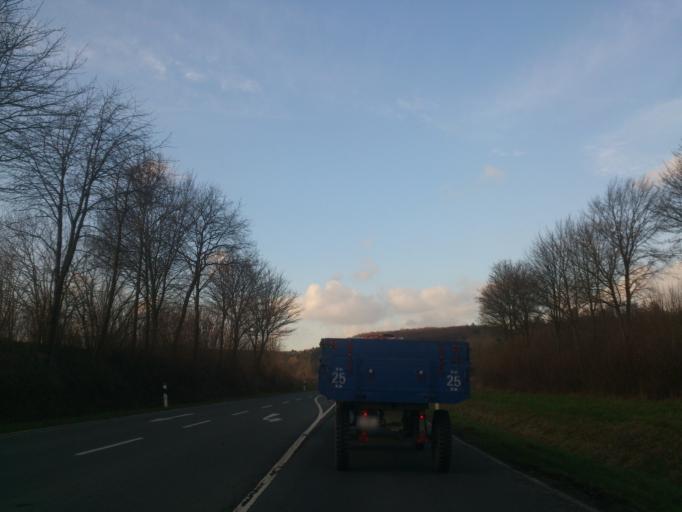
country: DE
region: North Rhine-Westphalia
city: Brakel
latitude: 51.7338
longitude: 9.1629
